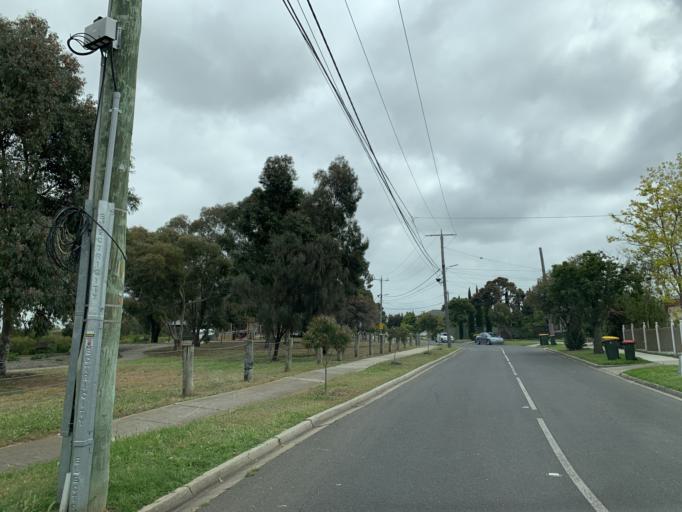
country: AU
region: Victoria
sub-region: Brimbank
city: Albion
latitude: -37.7611
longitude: 144.8548
